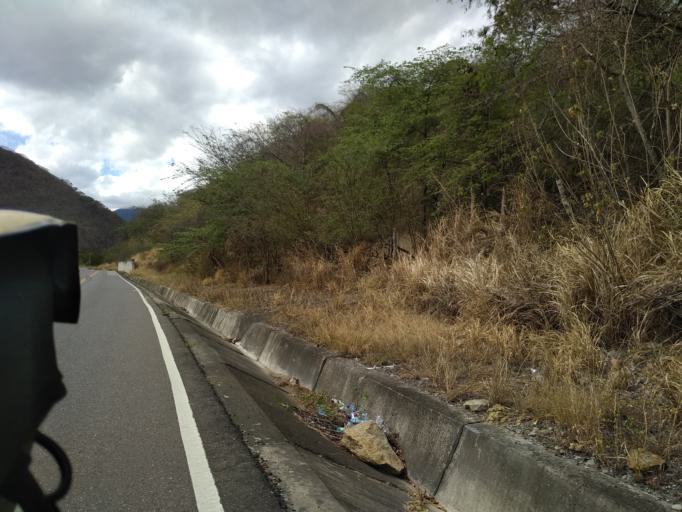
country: PE
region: Amazonas
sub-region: Utcubamba
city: Jamalca
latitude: -5.8687
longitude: -78.2172
